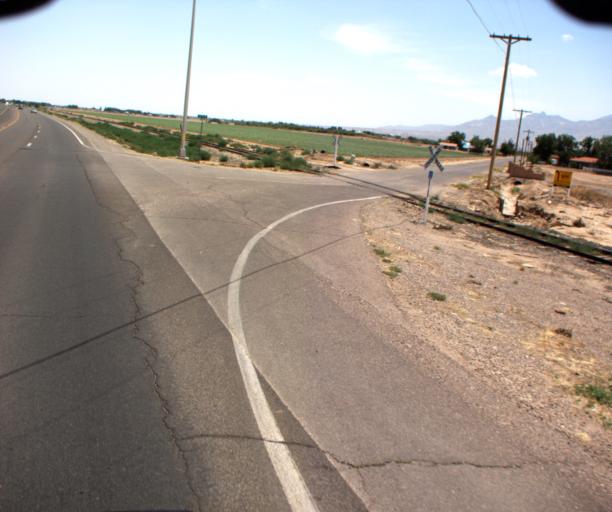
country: US
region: Arizona
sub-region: Graham County
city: Pima
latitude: 32.8869
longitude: -109.8144
